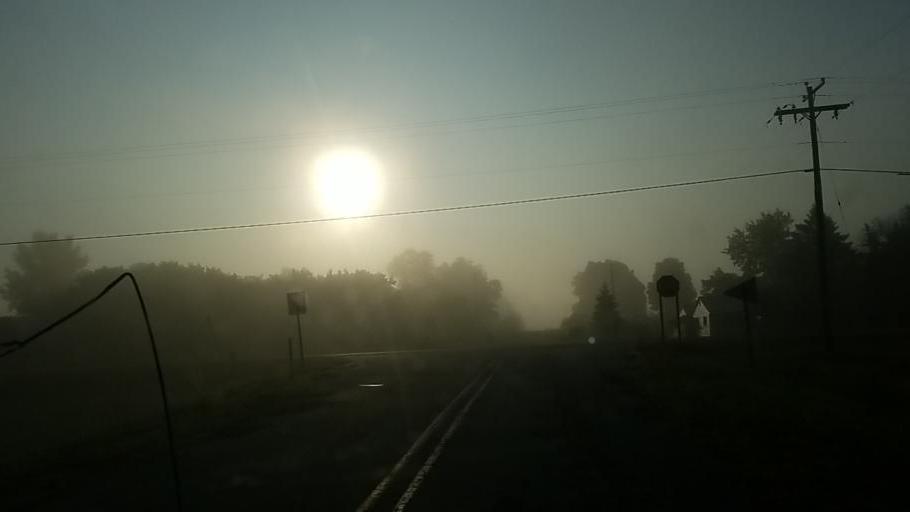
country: US
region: Michigan
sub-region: Newaygo County
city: Fremont
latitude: 43.4529
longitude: -86.0398
